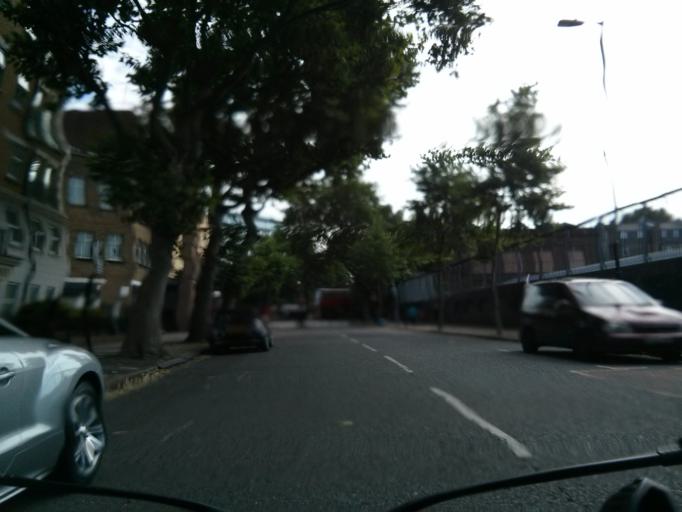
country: GB
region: England
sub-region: Greater London
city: Lambeth
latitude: 51.4981
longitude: -0.1058
